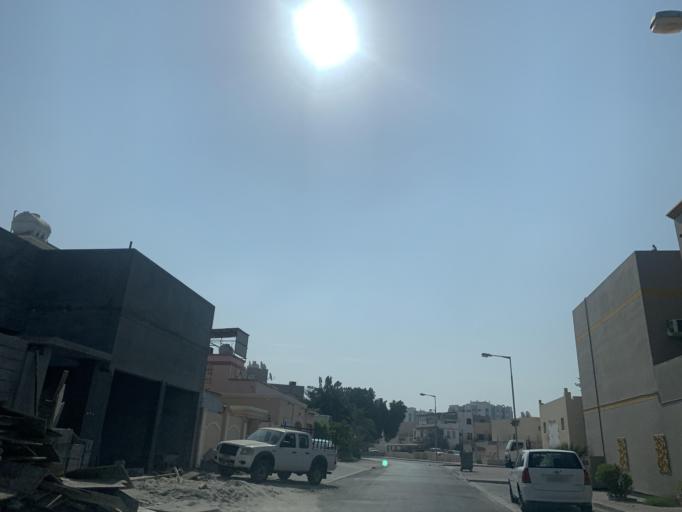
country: BH
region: Central Governorate
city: Madinat Hamad
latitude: 26.1182
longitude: 50.4914
